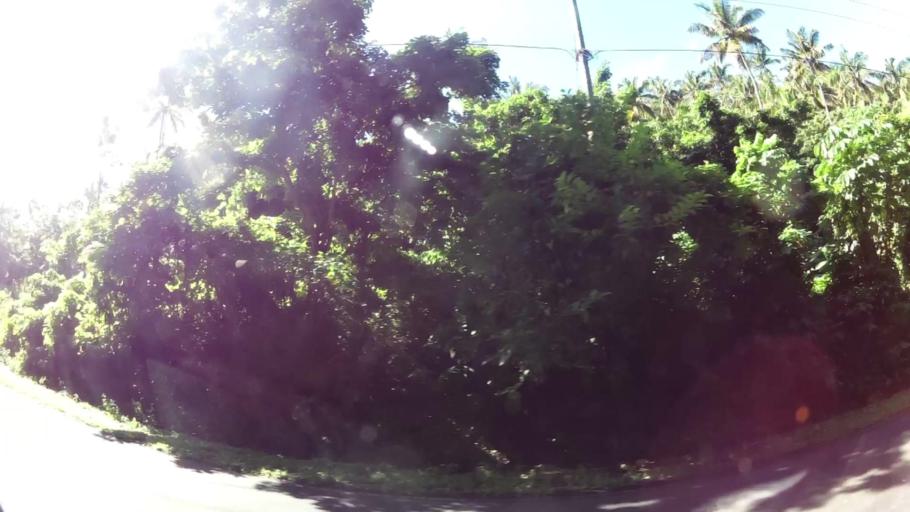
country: LC
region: Soufriere
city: Soufriere
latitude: 13.8446
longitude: -61.0519
